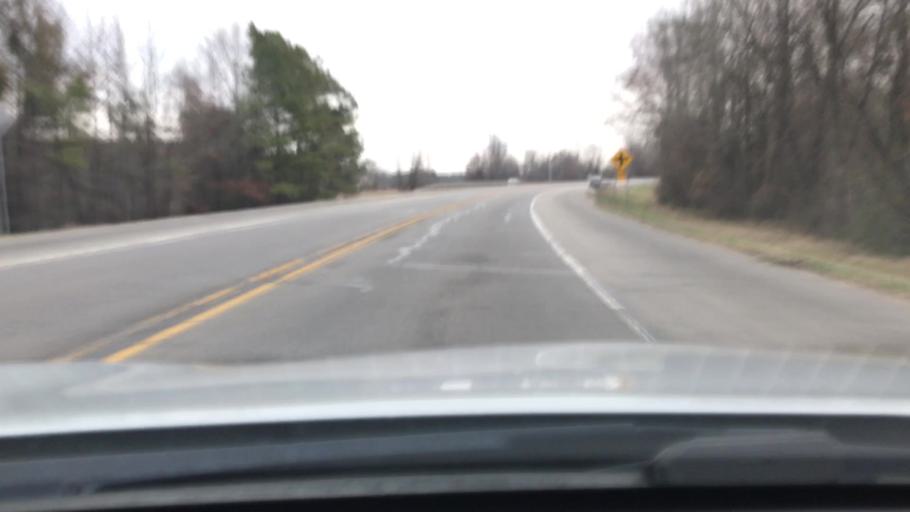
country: US
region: Arkansas
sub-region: Hempstead County
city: Hope
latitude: 33.6877
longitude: -93.5817
